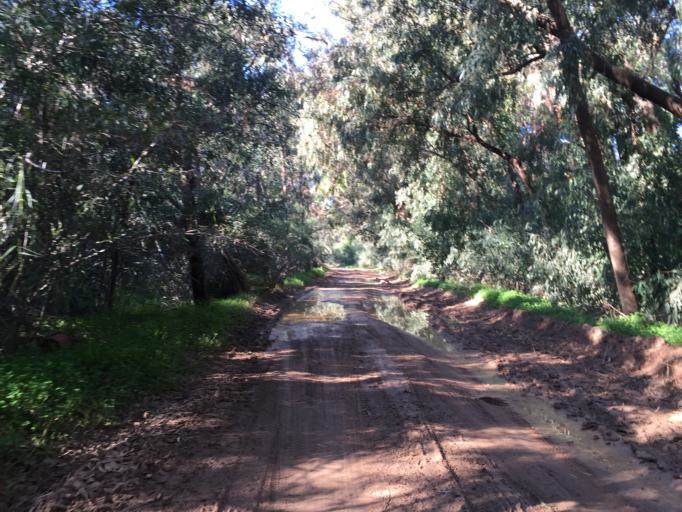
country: CY
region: Limassol
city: Ypsonas
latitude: 34.6432
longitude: 32.9968
